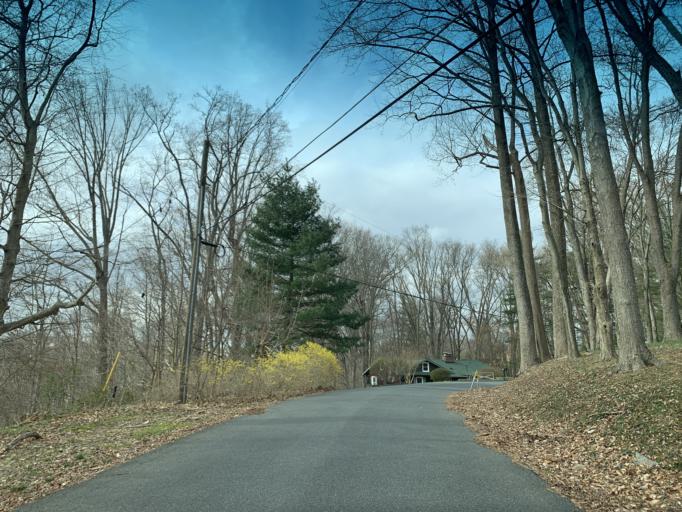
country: US
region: Maryland
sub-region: Harford County
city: North Bel Air
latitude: 39.5181
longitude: -76.3681
